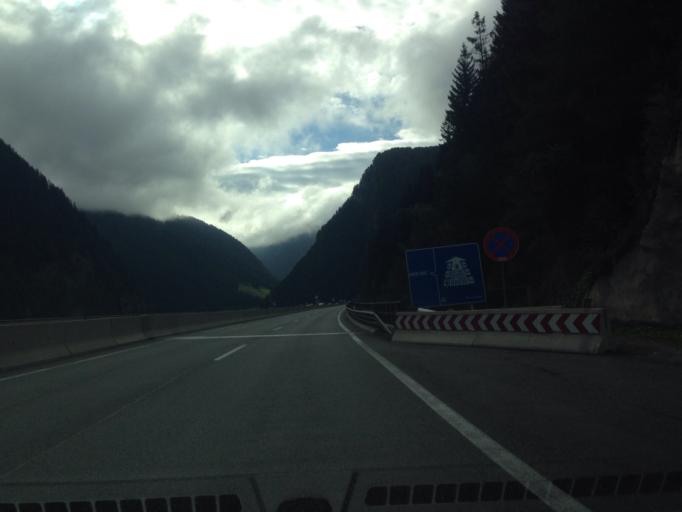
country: AT
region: Tyrol
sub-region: Politischer Bezirk Innsbruck Land
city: Gries am Brenner
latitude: 47.0326
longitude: 11.4837
